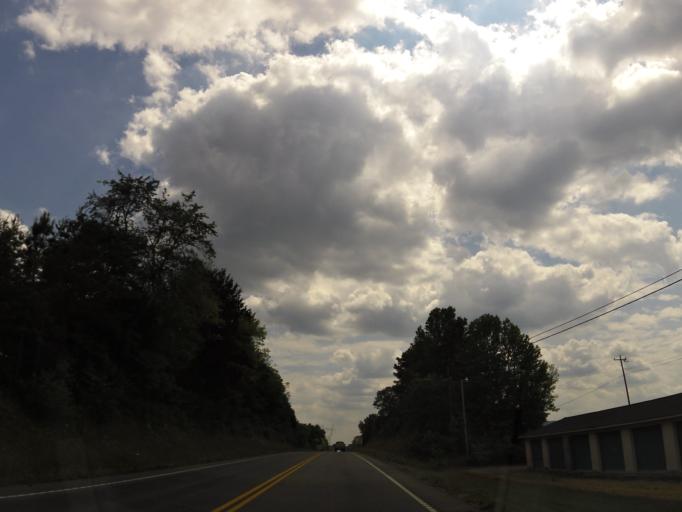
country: US
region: Tennessee
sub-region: Sequatchie County
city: Dunlap
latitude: 35.4373
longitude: -85.3488
